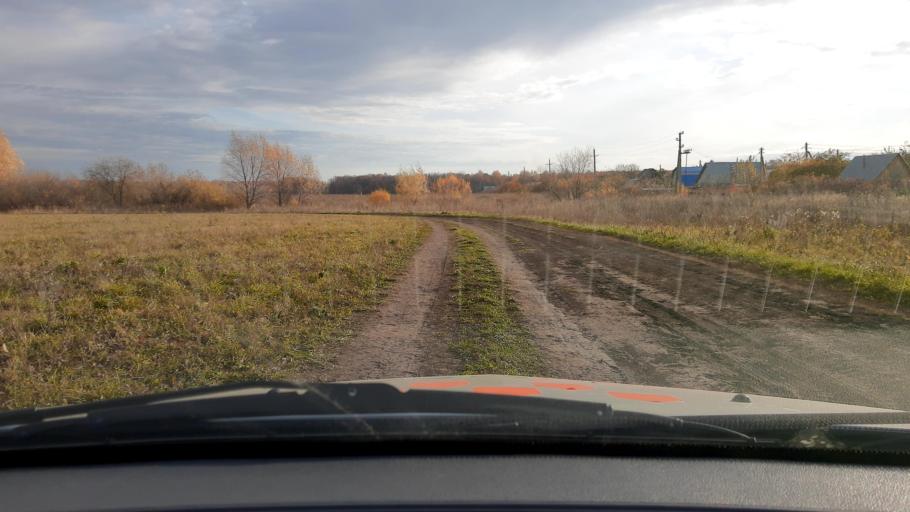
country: RU
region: Bashkortostan
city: Asanovo
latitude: 54.8066
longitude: 55.6102
